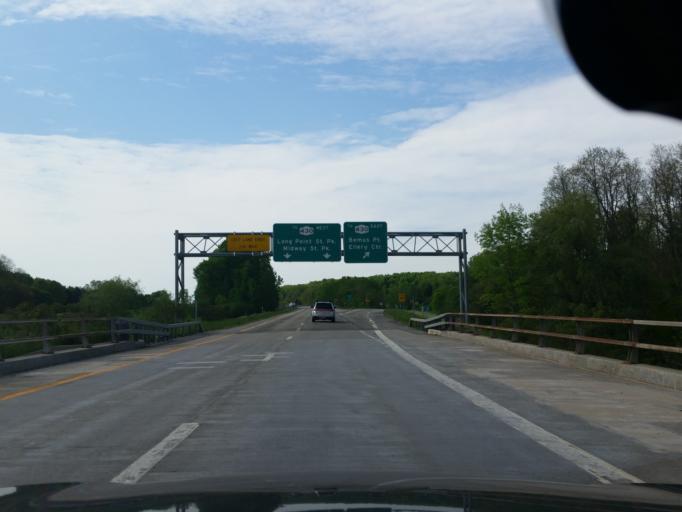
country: US
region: New York
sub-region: Chautauqua County
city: Lakewood
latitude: 42.1650
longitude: -79.3827
